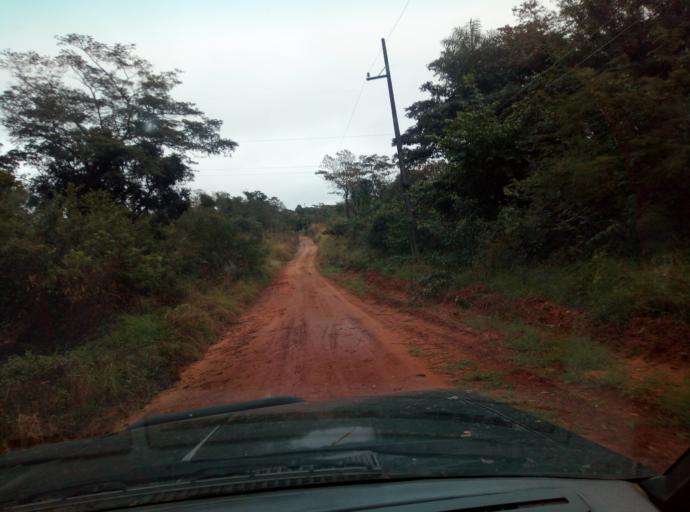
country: PY
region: Caaguazu
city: Carayao
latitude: -25.1904
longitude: -56.3581
